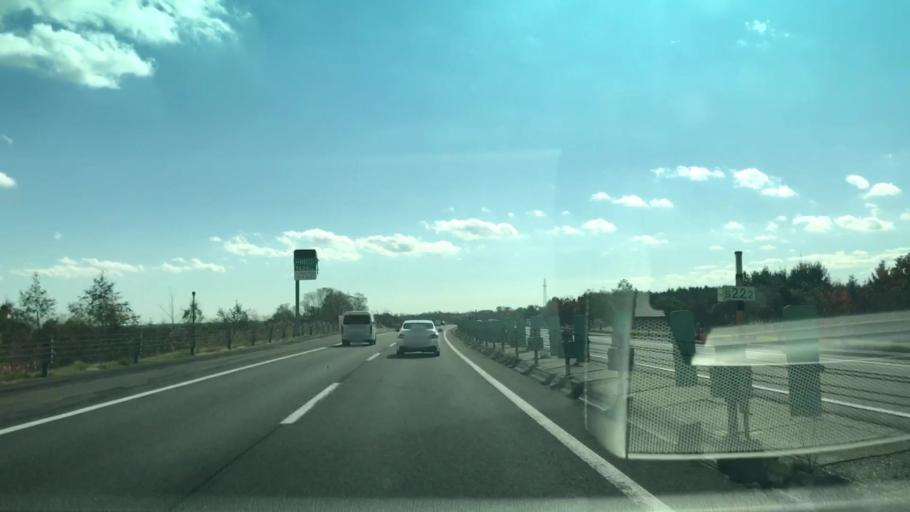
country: JP
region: Hokkaido
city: Kitahiroshima
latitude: 42.9075
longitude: 141.5506
